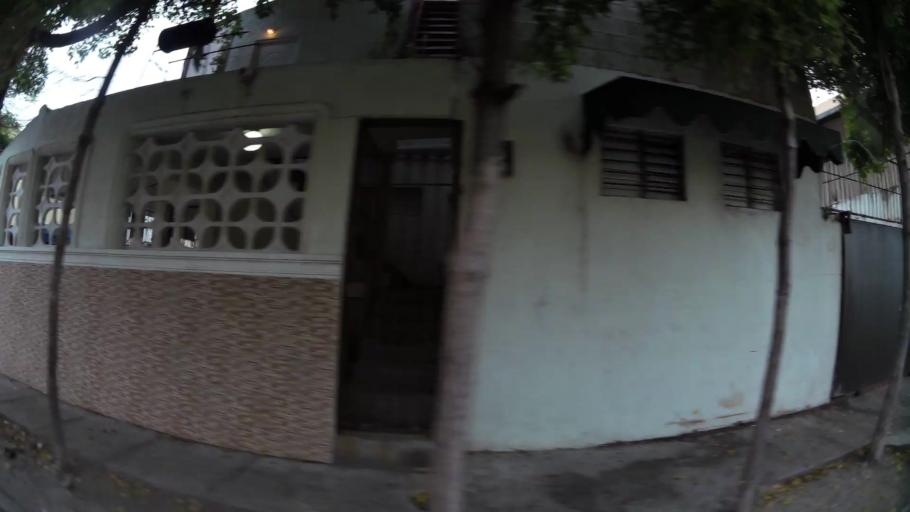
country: DO
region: Nacional
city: Bella Vista
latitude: 18.4415
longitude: -69.9312
